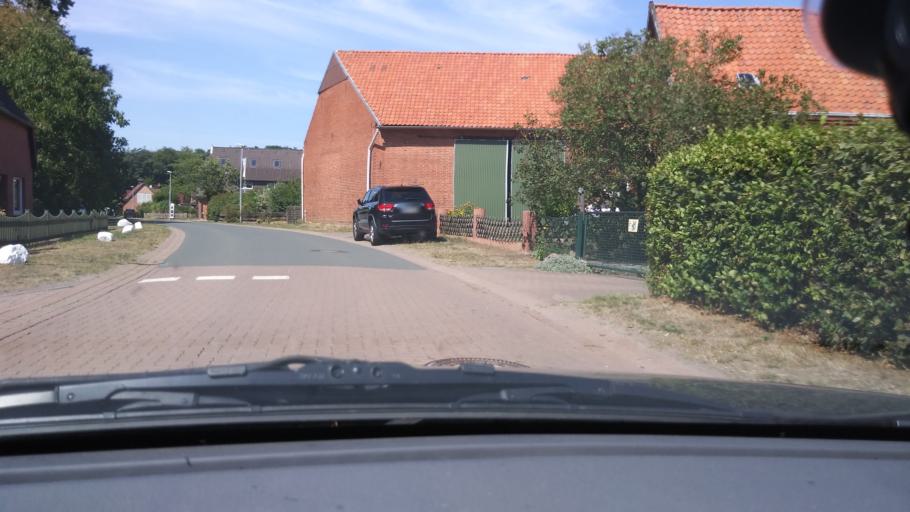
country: DE
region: Lower Saxony
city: Binnen
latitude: 52.6204
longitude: 9.1268
